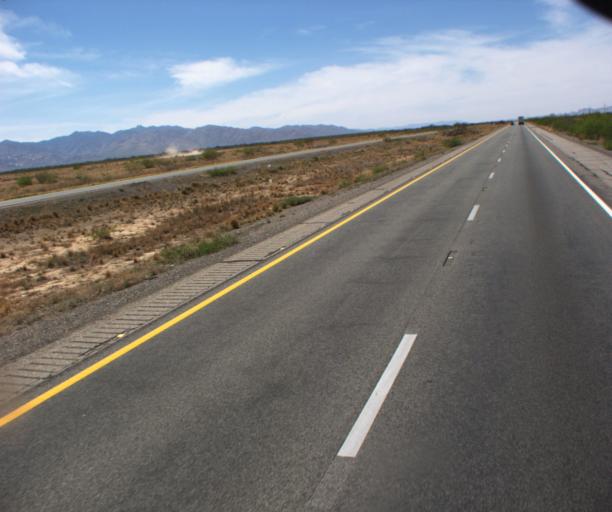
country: US
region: Arizona
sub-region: Cochise County
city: Willcox
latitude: 32.2983
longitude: -109.3573
